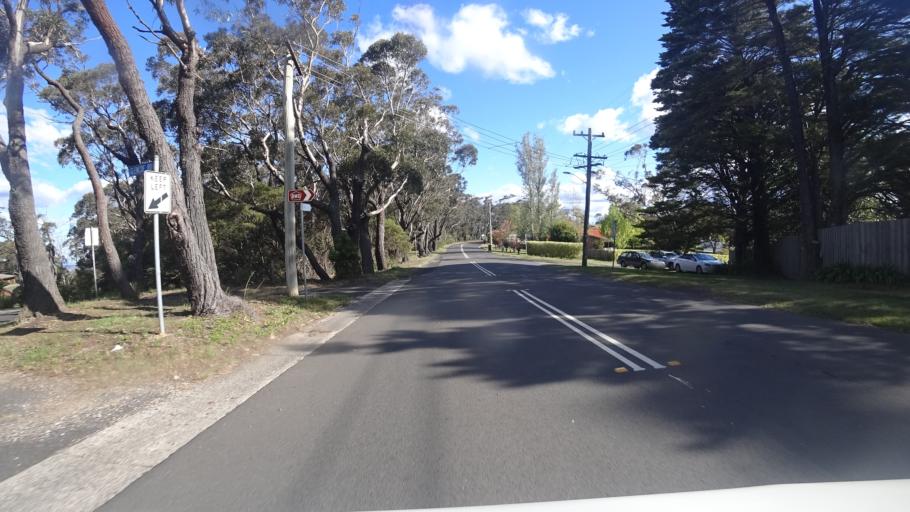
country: AU
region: New South Wales
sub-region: Blue Mountains Municipality
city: Katoomba
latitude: -33.7200
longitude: 150.2937
